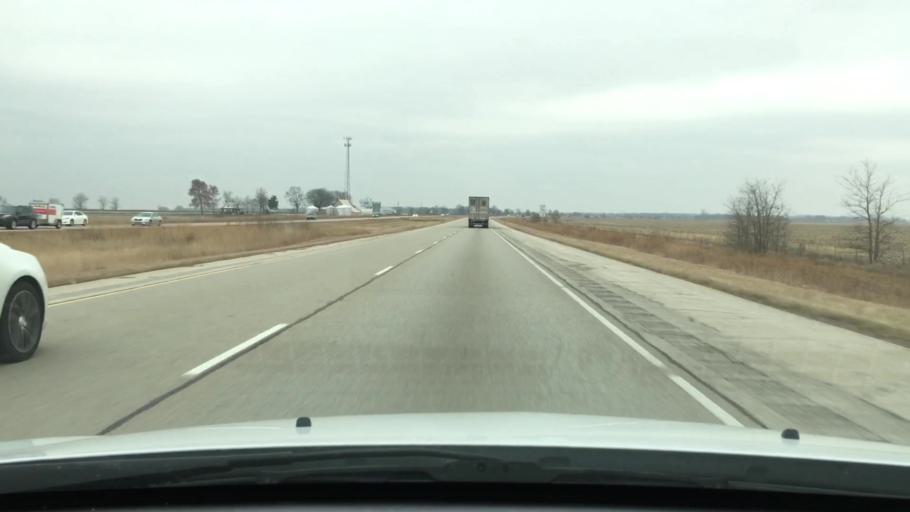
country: US
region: Illinois
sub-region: Logan County
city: Atlanta
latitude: 40.3196
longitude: -89.1579
